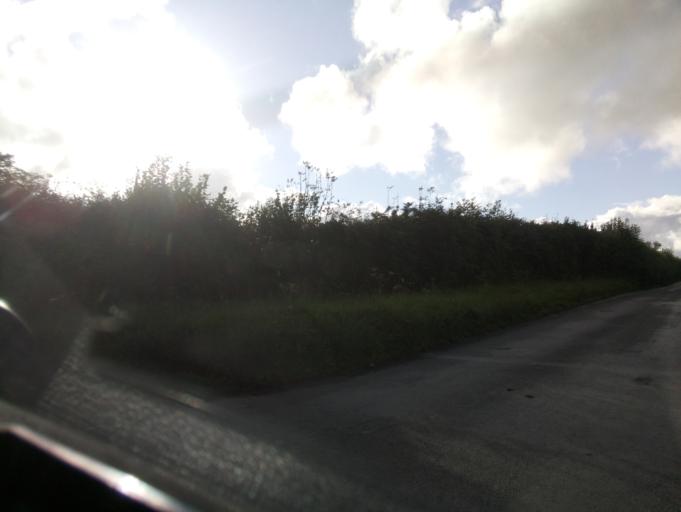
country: GB
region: England
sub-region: Devon
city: South Brent
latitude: 50.3917
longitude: -3.7727
